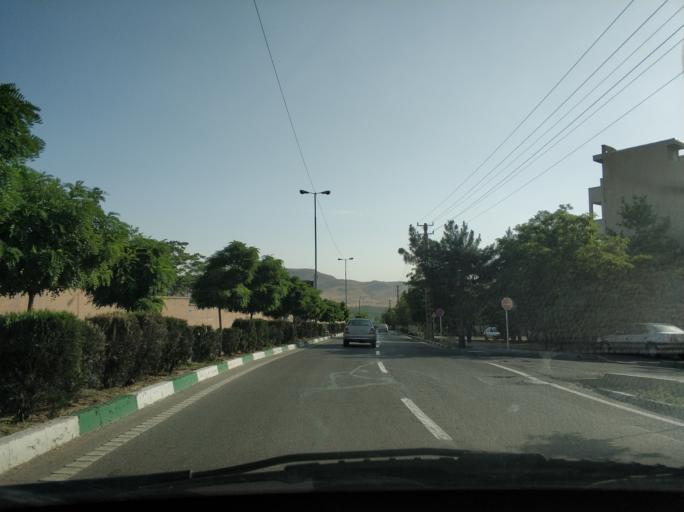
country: IR
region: Tehran
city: Tehran
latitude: 35.7290
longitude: 51.5920
